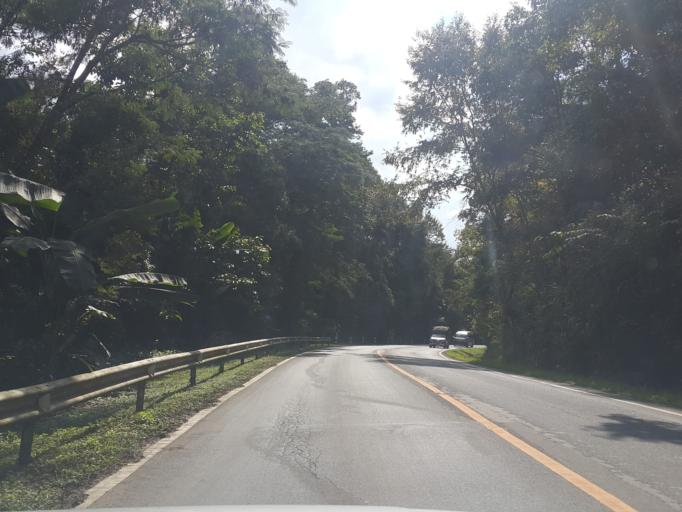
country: TH
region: Chiang Mai
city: Mae Chaem
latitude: 18.5453
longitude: 98.5352
